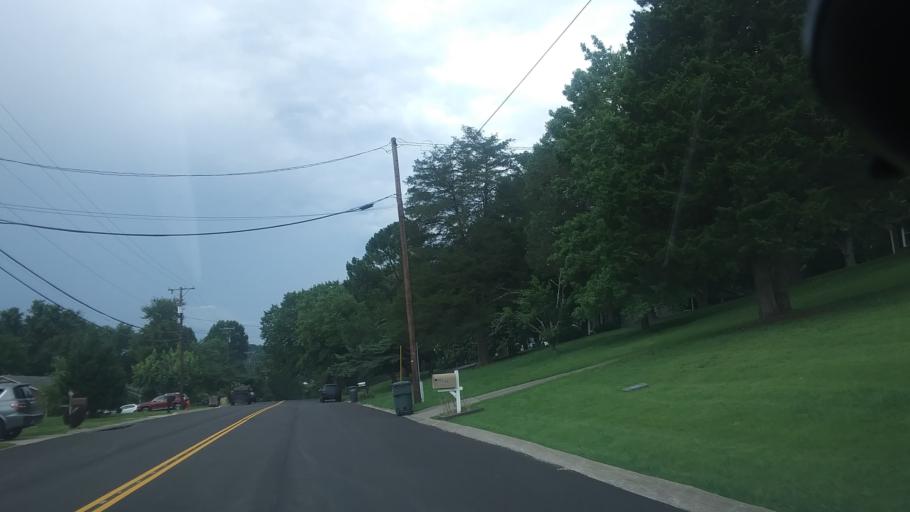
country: US
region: Tennessee
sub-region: Davidson County
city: Belle Meade
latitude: 36.0818
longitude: -86.9371
